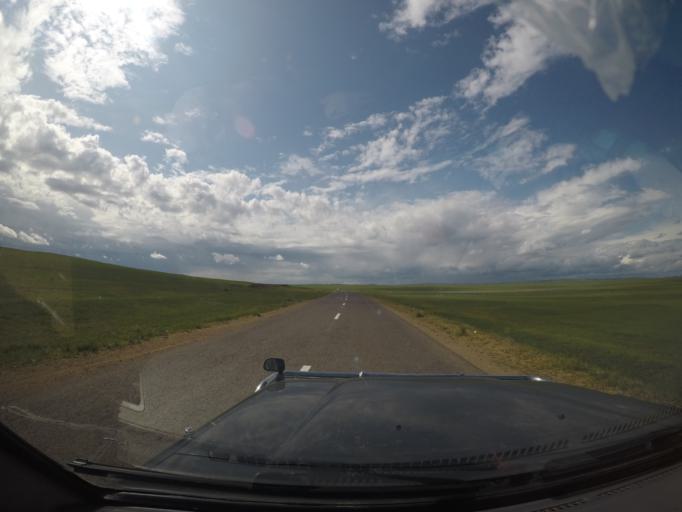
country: MN
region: Hentiy
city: Bayanbulag
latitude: 47.4573
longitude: 109.6746
